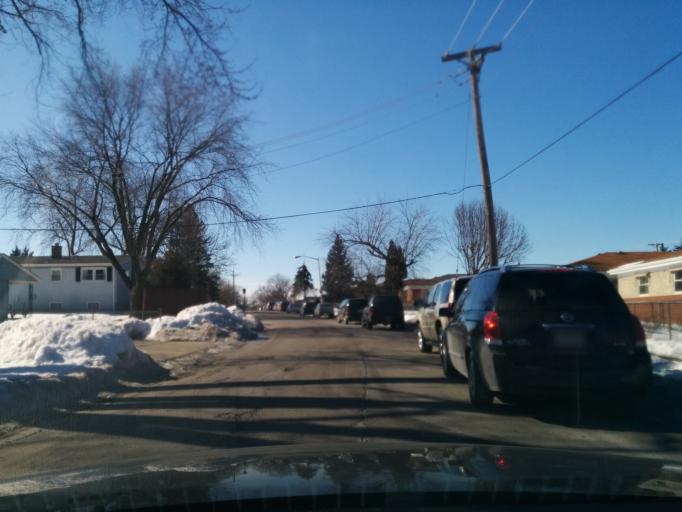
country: US
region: Illinois
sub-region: DuPage County
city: Villa Park
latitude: 41.8944
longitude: -87.9891
